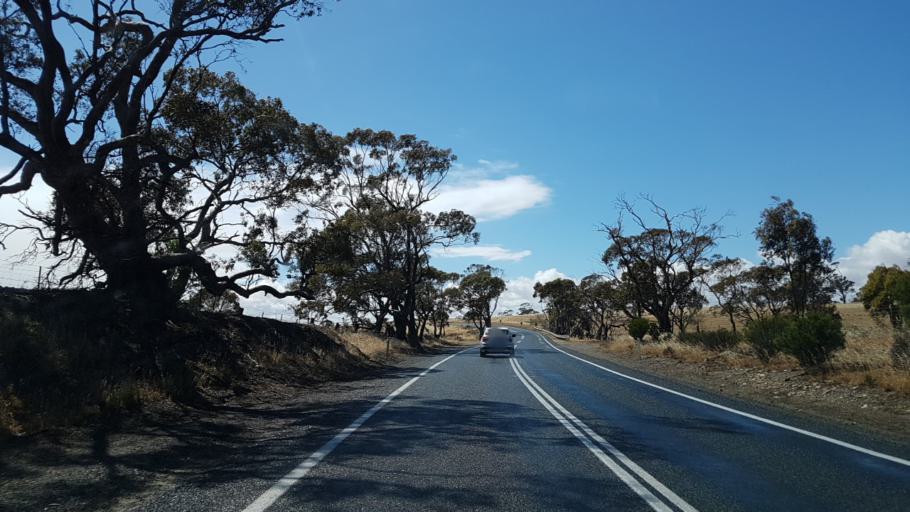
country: AU
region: South Australia
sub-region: Barossa
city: Angaston
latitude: -34.3997
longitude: 139.1750
